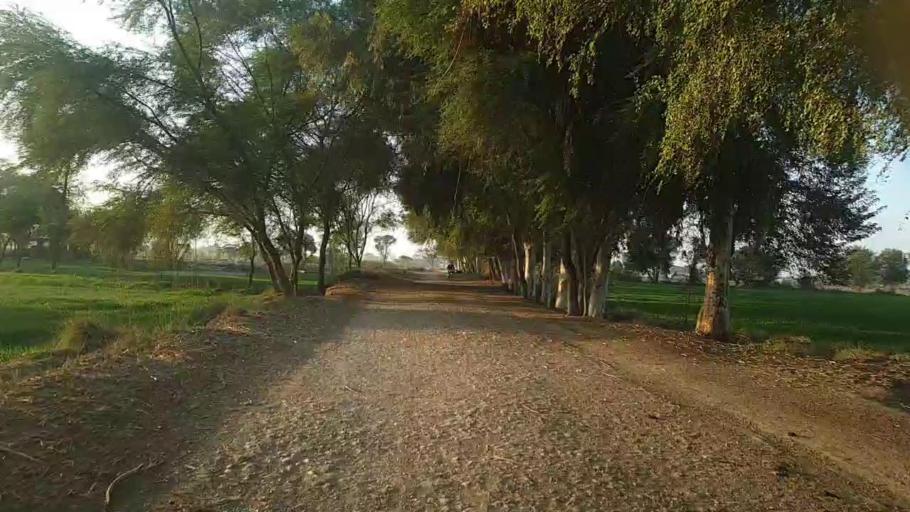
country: PK
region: Sindh
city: Mirpur Mathelo
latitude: 27.8926
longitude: 69.6576
